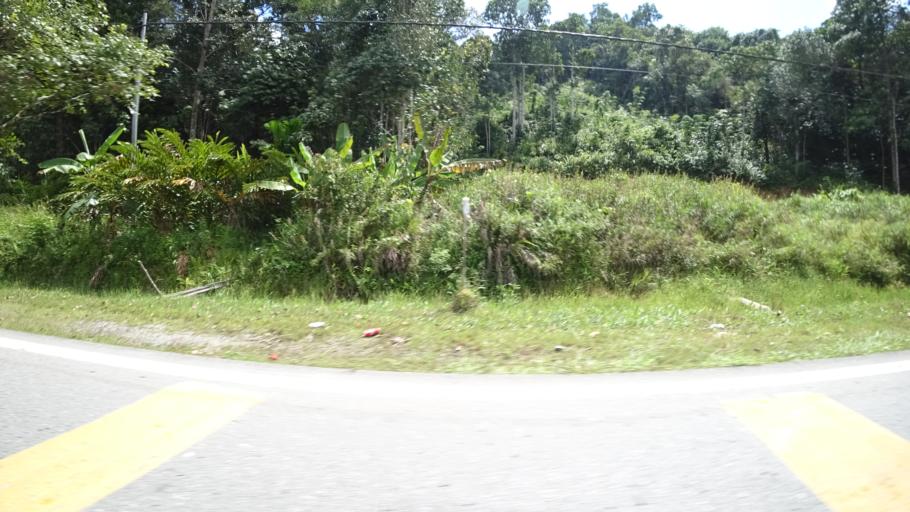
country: MY
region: Sarawak
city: Limbang
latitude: 4.6985
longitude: 114.9842
